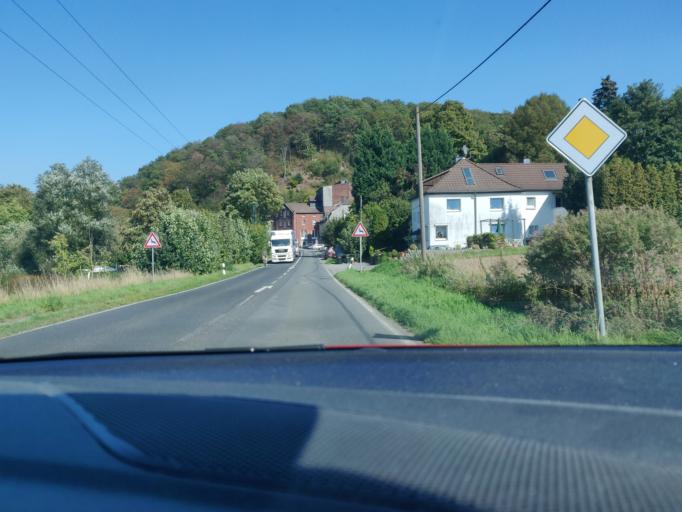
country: DE
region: North Rhine-Westphalia
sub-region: Regierungsbezirk Dusseldorf
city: Velbert
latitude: 51.3372
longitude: 7.0964
